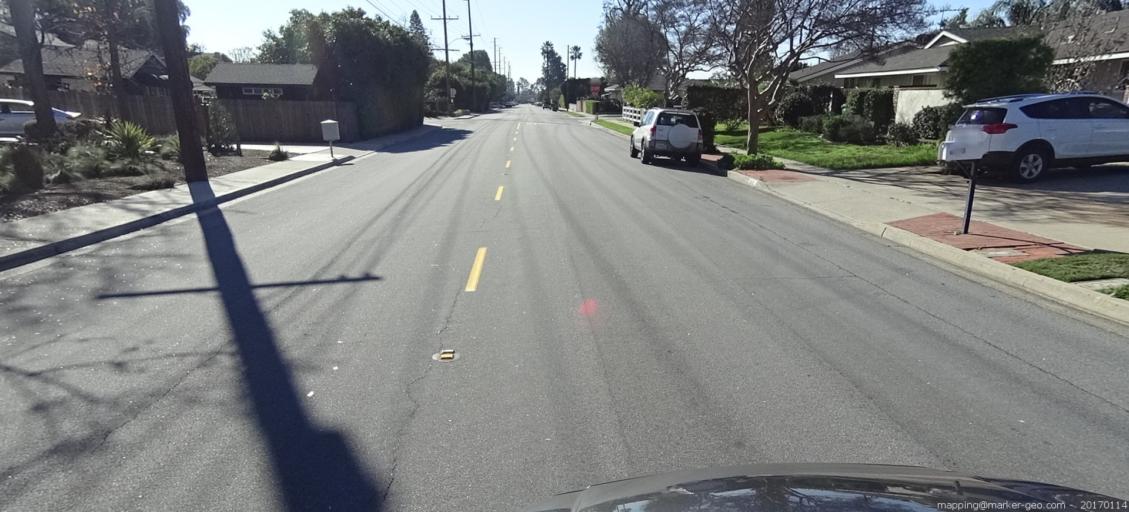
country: US
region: California
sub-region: Orange County
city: North Tustin
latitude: 33.7637
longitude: -117.8060
